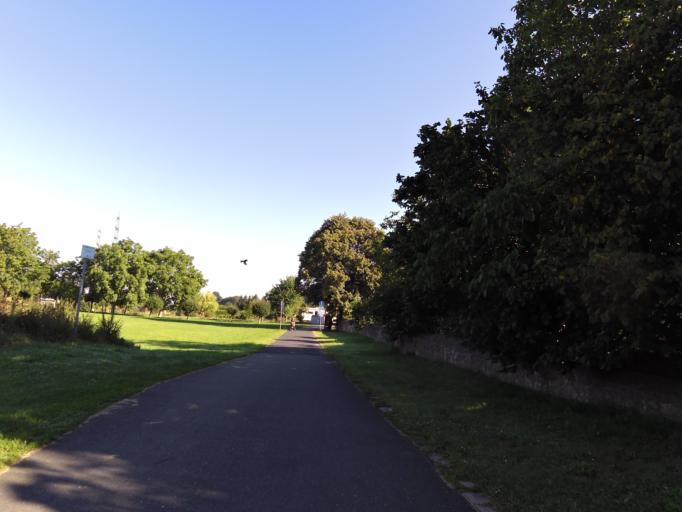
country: DE
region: Saxony
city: Weissig
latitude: 51.2402
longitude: 13.4143
